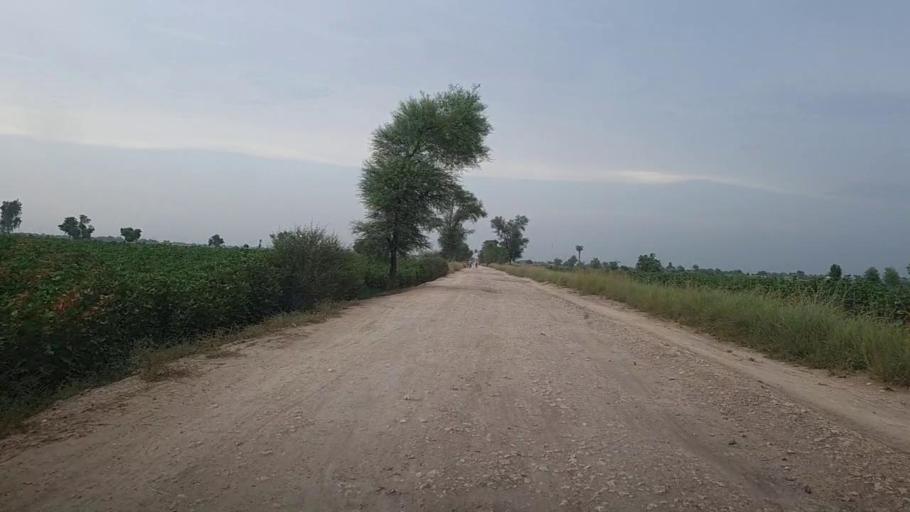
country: PK
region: Sindh
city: Karaundi
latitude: 26.9633
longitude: 68.3438
